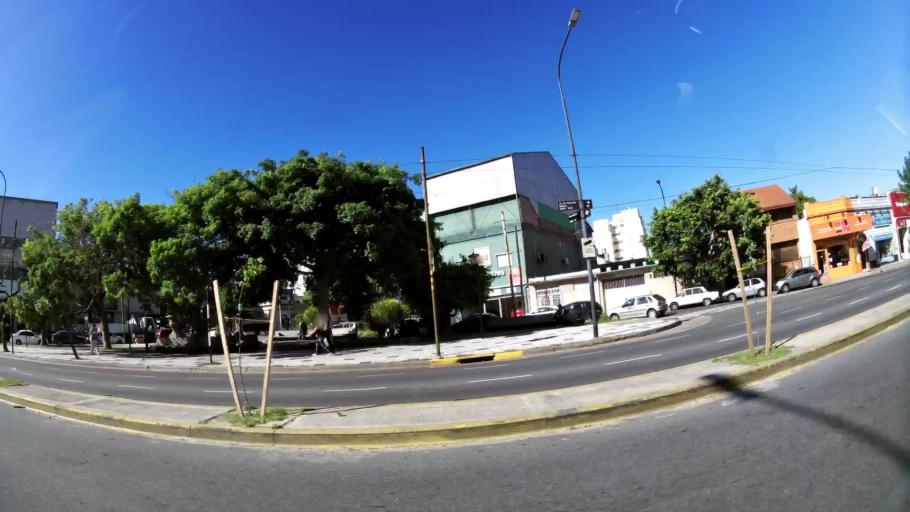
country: AR
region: Buenos Aires F.D.
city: Colegiales
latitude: -34.5559
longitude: -58.4818
